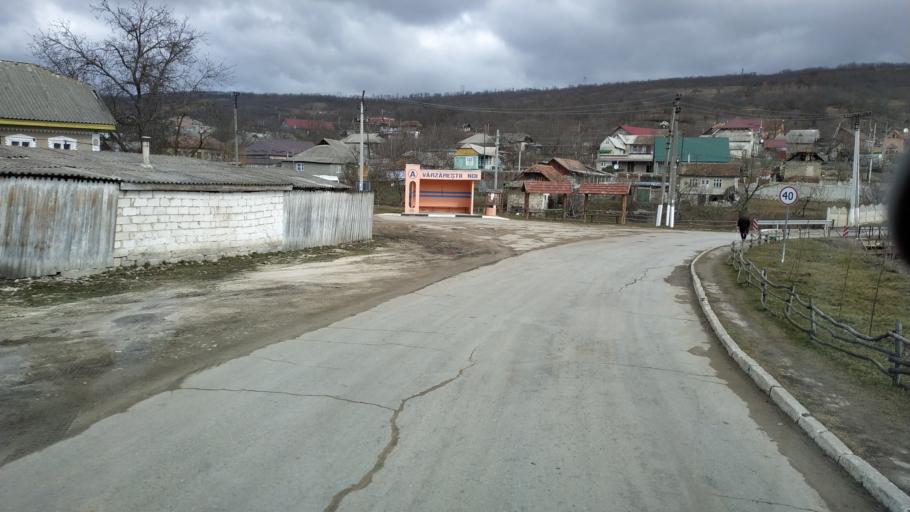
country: MD
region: Stinga Nistrului
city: Bucovat
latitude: 47.2326
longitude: 28.4432
